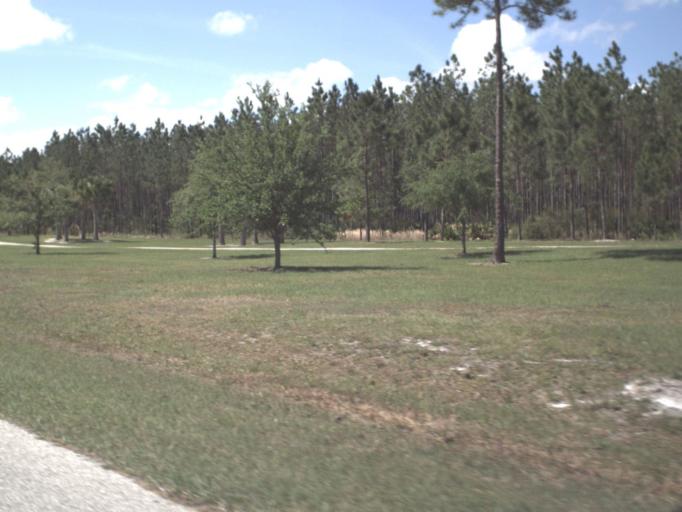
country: US
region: Florida
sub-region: Flagler County
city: Palm Coast
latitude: 29.6219
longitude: -81.2823
